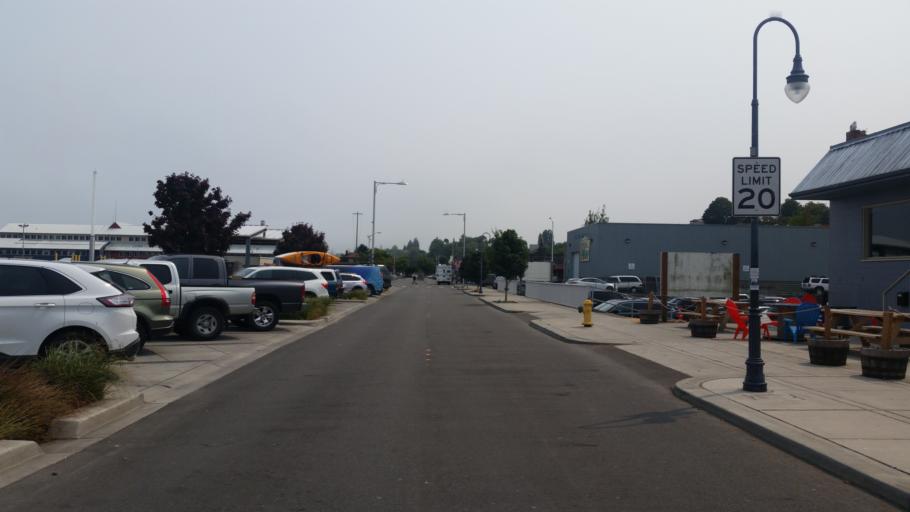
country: US
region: Washington
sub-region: Clallam County
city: Port Angeles
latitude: 48.1212
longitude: -123.4332
